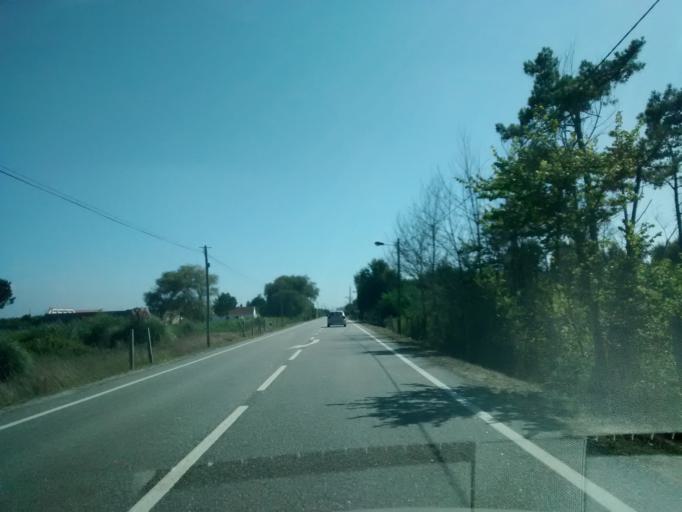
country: PT
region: Aveiro
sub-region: Ilhavo
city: Gafanha da Nazare
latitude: 40.6692
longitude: -8.7260
